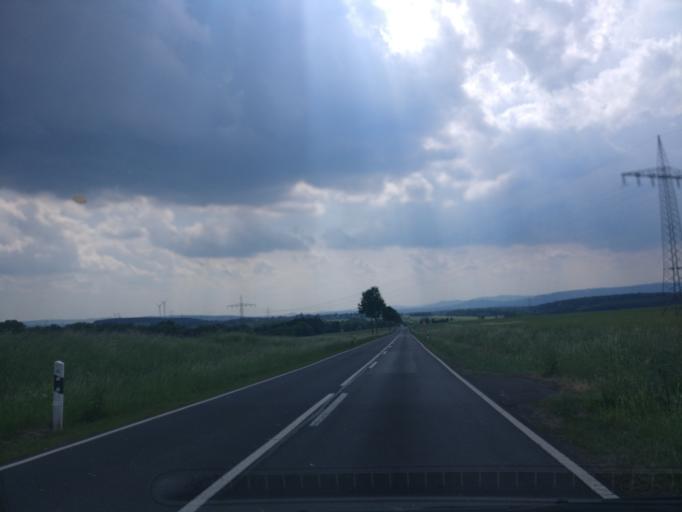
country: DE
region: Hesse
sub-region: Regierungsbezirk Kassel
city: Fuldatal
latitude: 51.3712
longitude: 9.6117
